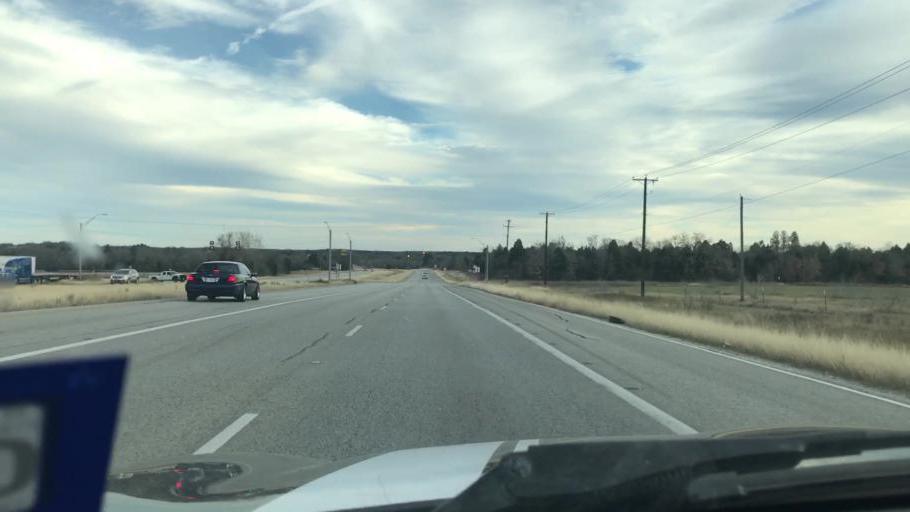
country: US
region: Texas
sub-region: Bastrop County
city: Elgin
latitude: 30.3115
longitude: -97.3065
